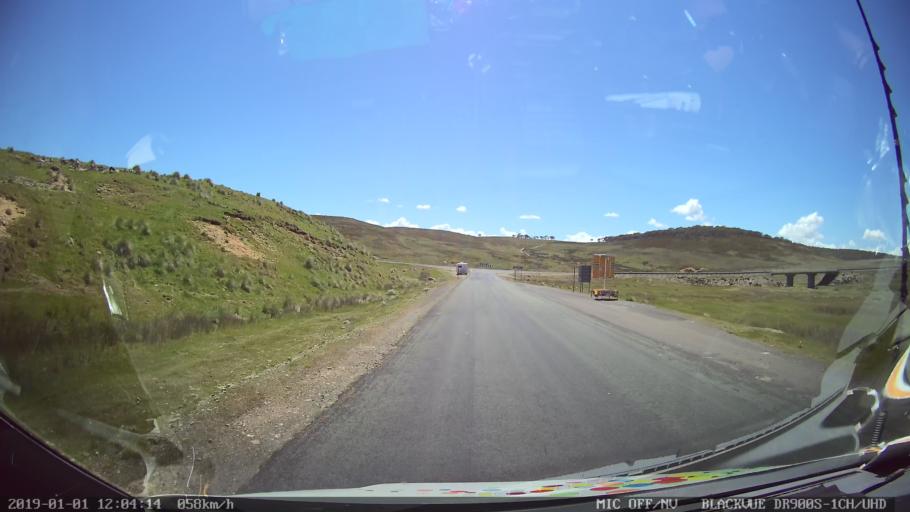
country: AU
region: New South Wales
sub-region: Snowy River
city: Jindabyne
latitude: -35.8668
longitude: 148.4944
